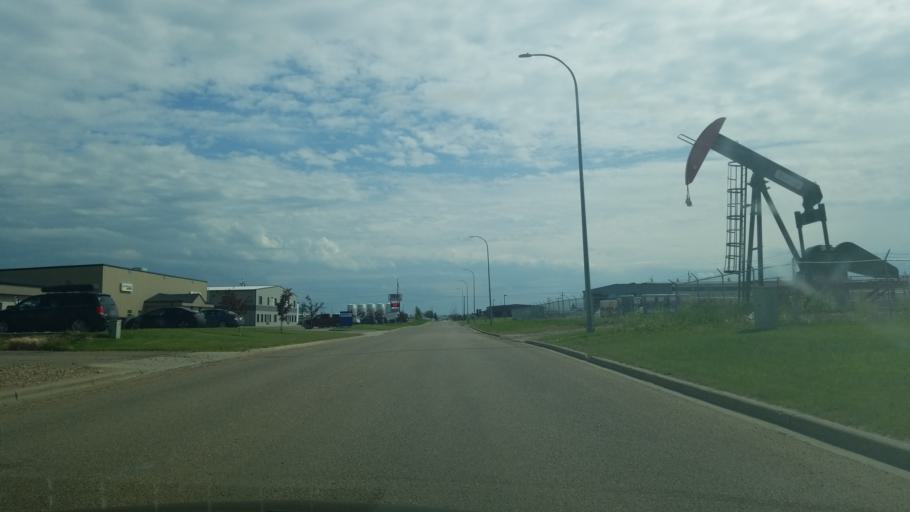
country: CA
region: Saskatchewan
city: Lloydminster
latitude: 53.2954
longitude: -110.0367
